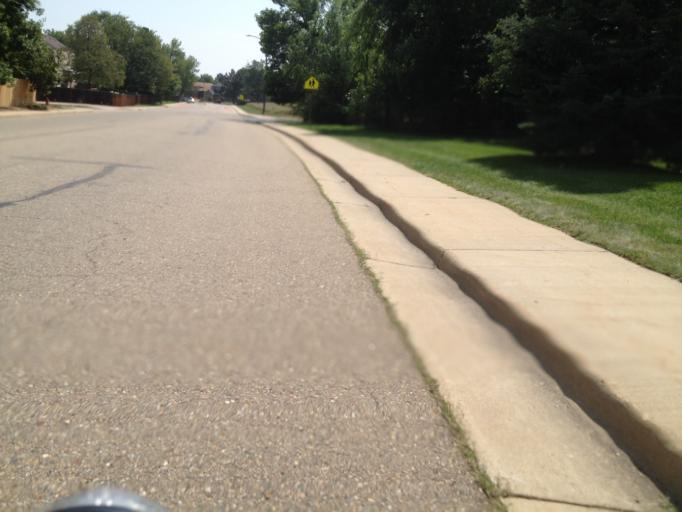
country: US
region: Colorado
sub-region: Boulder County
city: Louisville
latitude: 39.9737
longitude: -105.1424
